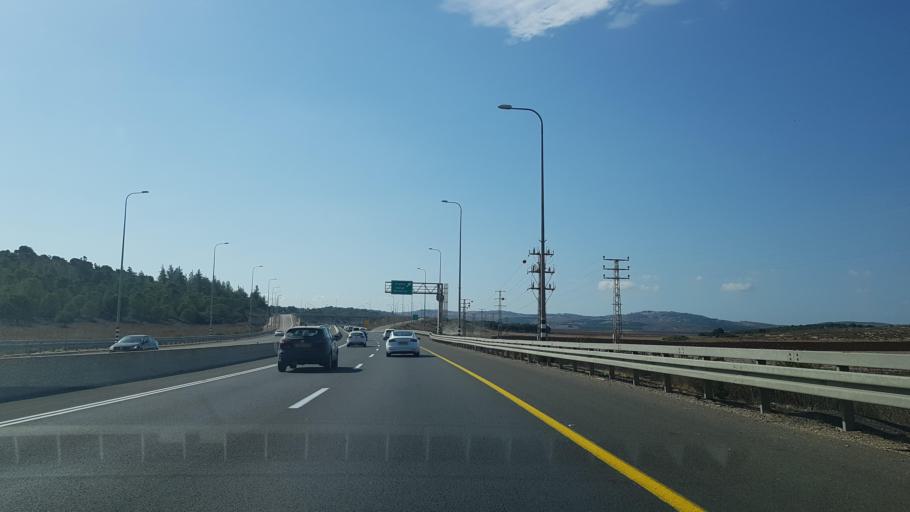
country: IL
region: Northern District
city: Rumat Heib
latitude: 32.7699
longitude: 35.2996
